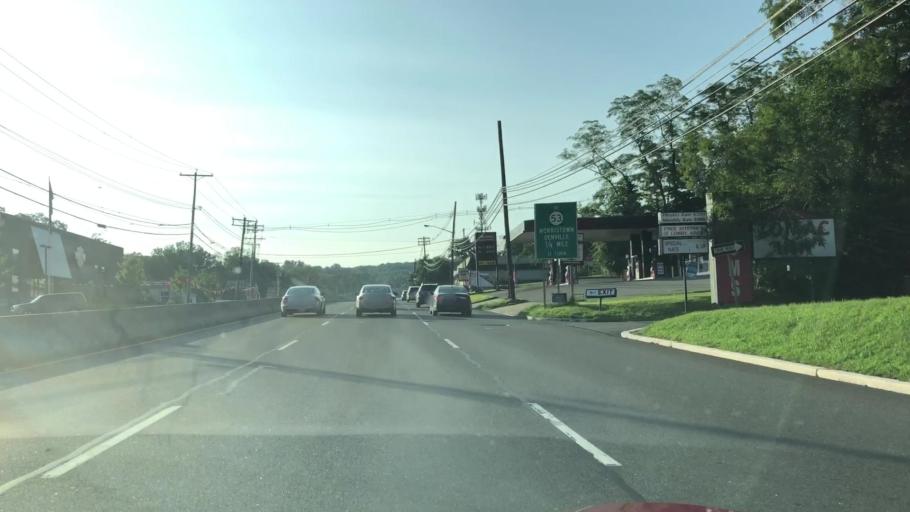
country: US
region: New Jersey
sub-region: Morris County
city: Morris Plains
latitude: 40.8485
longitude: -74.4701
